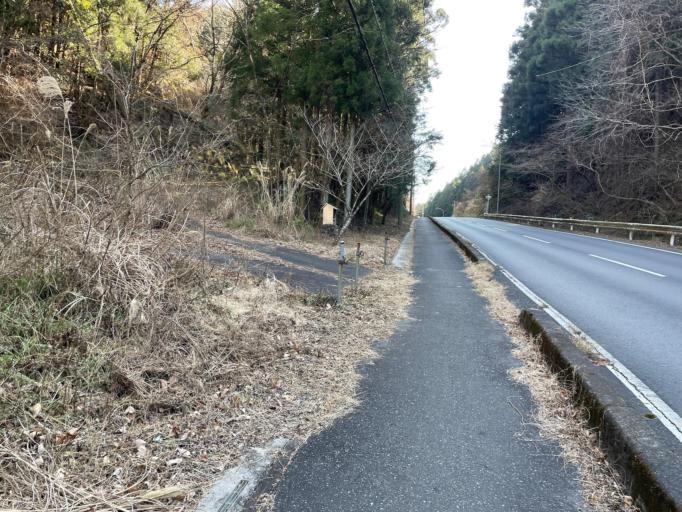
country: JP
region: Tokyo
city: Ome
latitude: 35.8580
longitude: 139.2428
